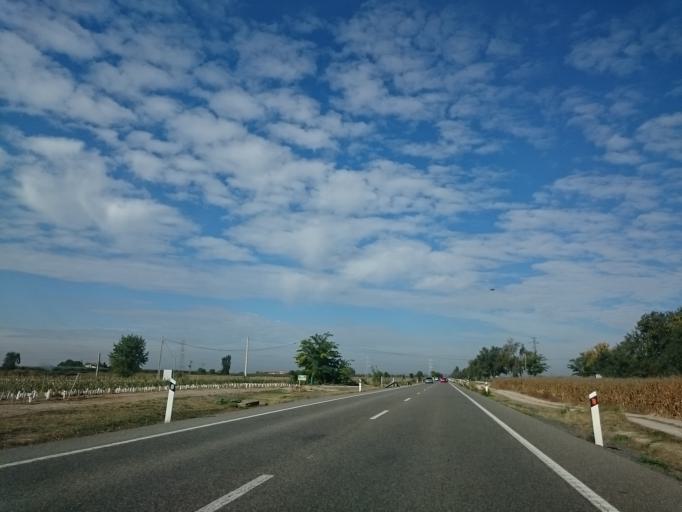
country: ES
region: Catalonia
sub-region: Provincia de Lleida
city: Juneda
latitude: 41.5767
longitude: 0.7577
